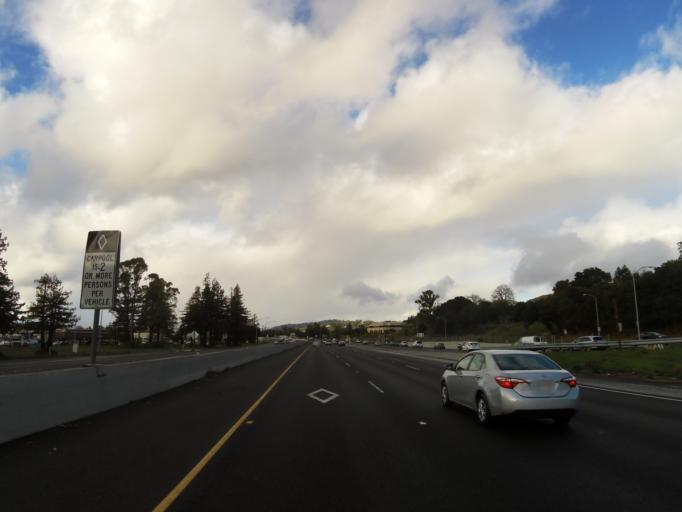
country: US
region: California
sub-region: Sonoma County
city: Santa Rosa
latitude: 38.4750
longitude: -122.7313
